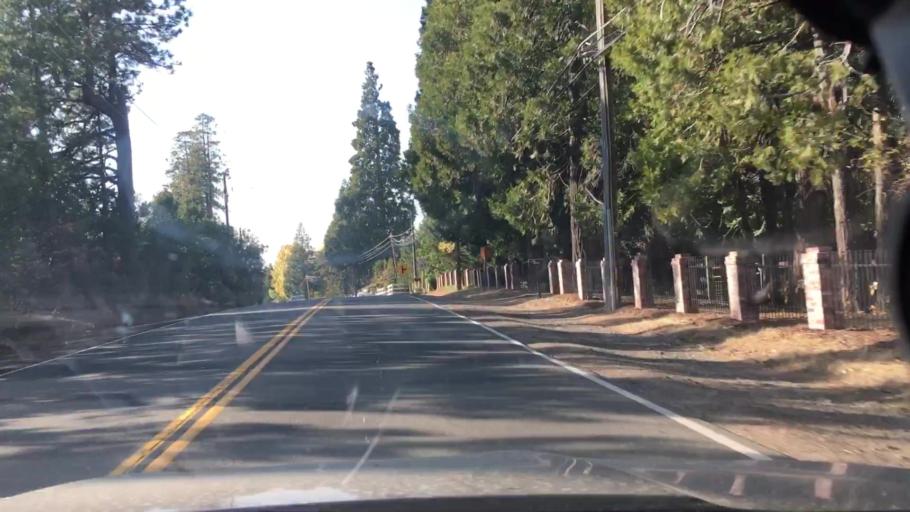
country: US
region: California
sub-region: El Dorado County
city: Camino
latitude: 38.7408
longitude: -120.6923
